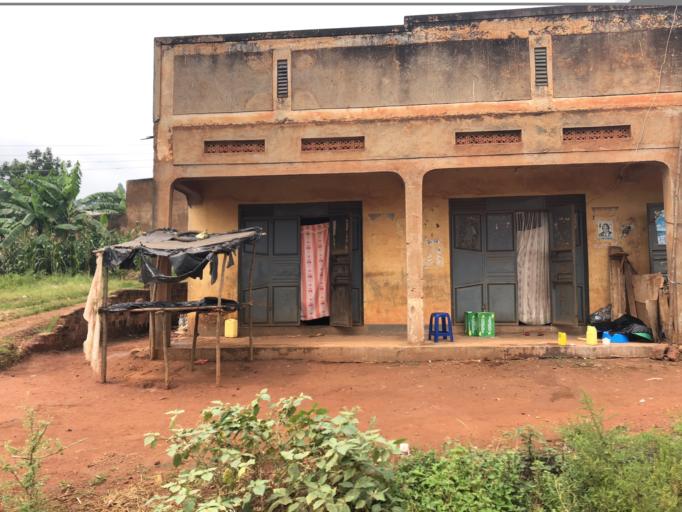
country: UG
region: Central Region
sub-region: Mukono District
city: Mukono
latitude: 0.3517
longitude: 32.7505
